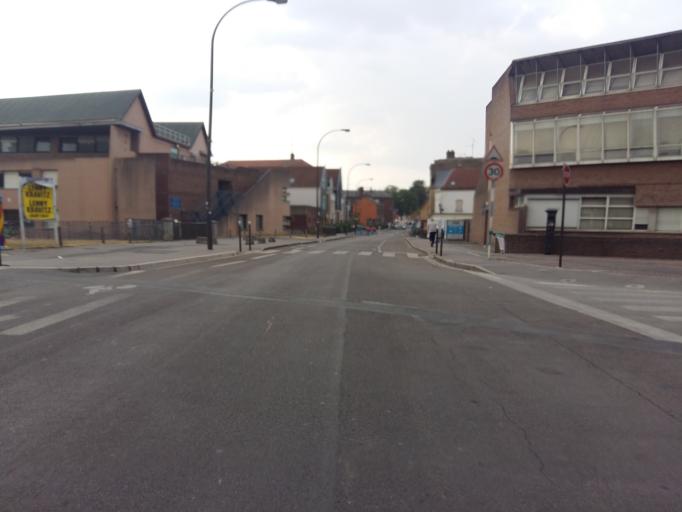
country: FR
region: Picardie
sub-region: Departement de la Somme
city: Amiens
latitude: 49.8996
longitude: 2.3004
